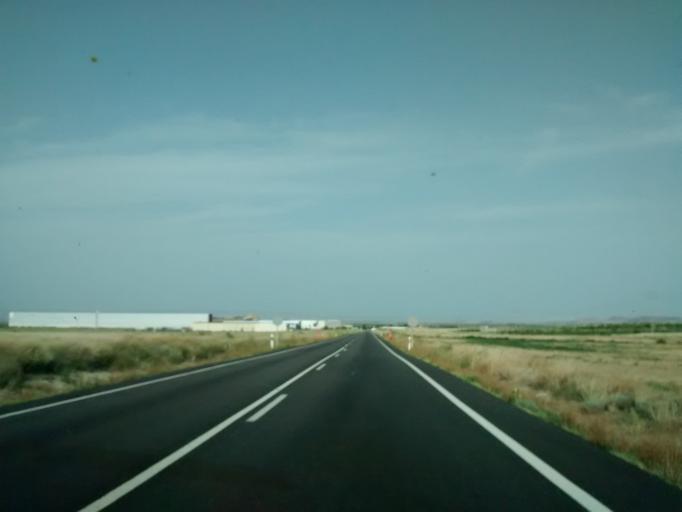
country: ES
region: Aragon
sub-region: Provincia de Zaragoza
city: Albeta
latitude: 41.8307
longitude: -1.4939
